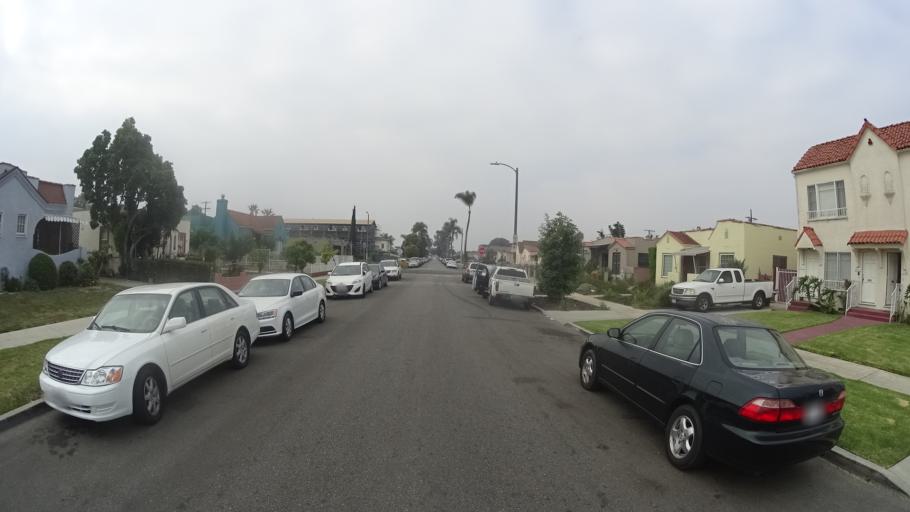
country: US
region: California
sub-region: Los Angeles County
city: View Park-Windsor Hills
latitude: 34.0300
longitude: -118.3317
